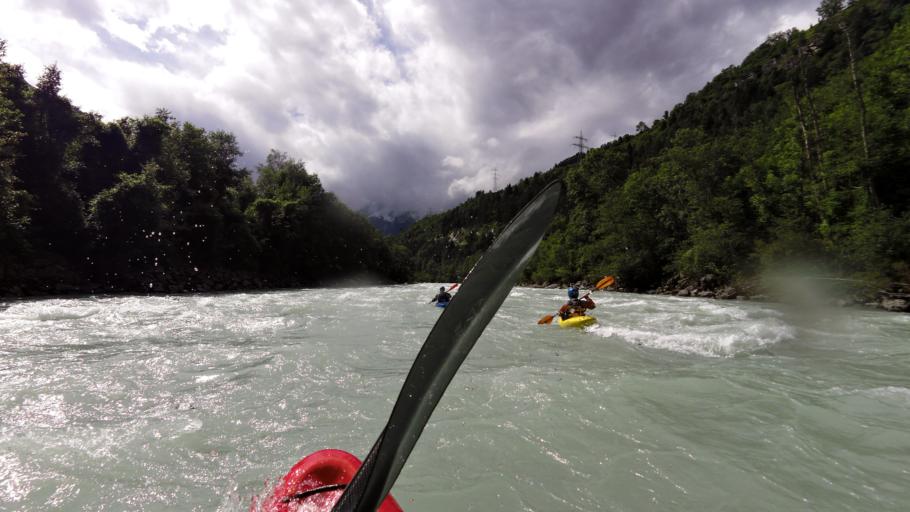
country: AT
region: Tyrol
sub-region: Politischer Bezirk Landeck
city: Zams
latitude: 47.1218
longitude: 10.5993
